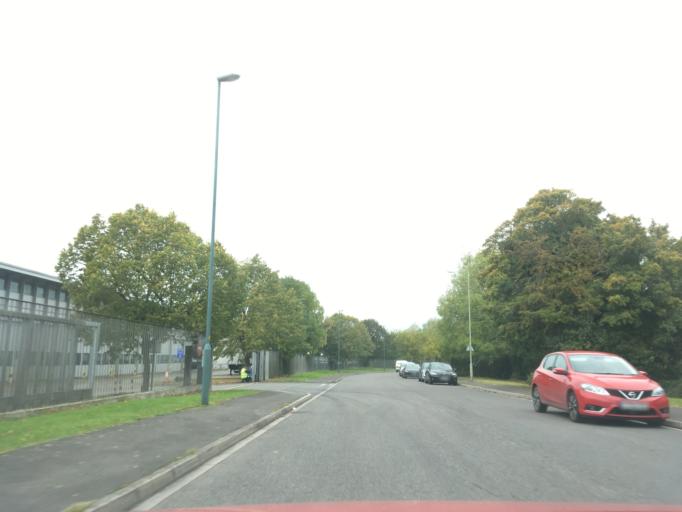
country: GB
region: England
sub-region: Gloucestershire
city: Stonehouse
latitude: 51.7492
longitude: -2.2989
